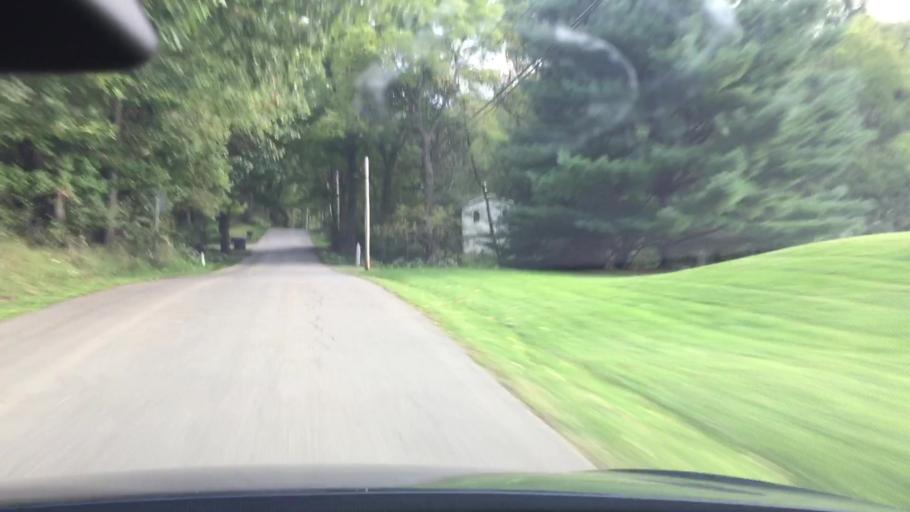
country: US
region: Pennsylvania
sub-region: Allegheny County
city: Curtisville
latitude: 40.6942
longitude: -79.8771
